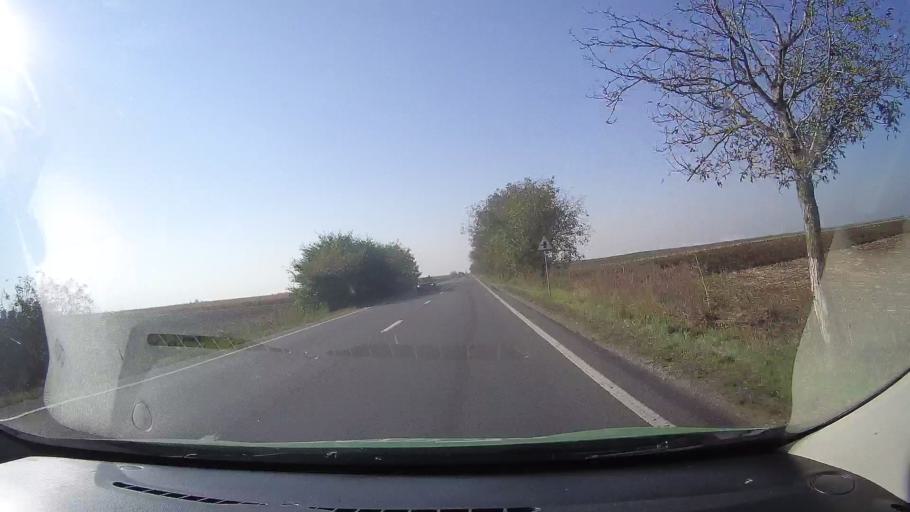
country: RO
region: Satu Mare
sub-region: Comuna Petresti
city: Petresti
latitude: 47.6262
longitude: 22.3880
